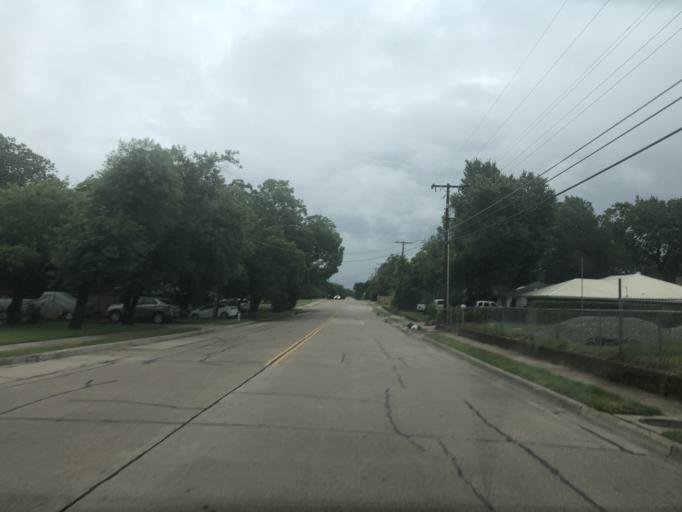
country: US
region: Texas
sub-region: Dallas County
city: Irving
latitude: 32.7939
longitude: -96.9423
